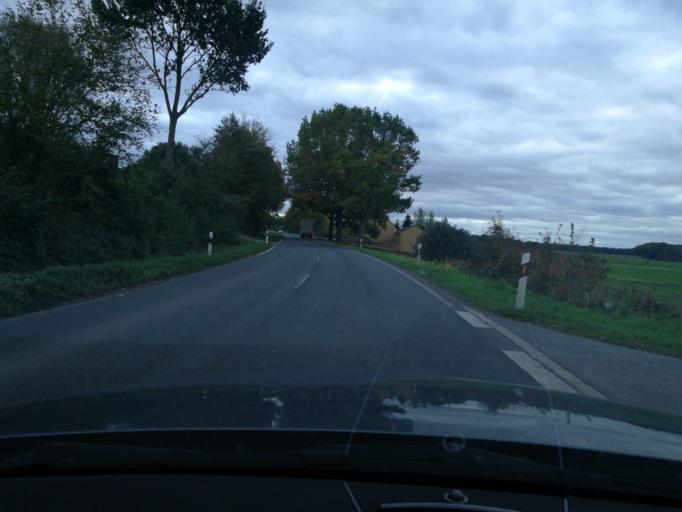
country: DE
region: North Rhine-Westphalia
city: Straelen
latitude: 51.4324
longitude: 6.2419
